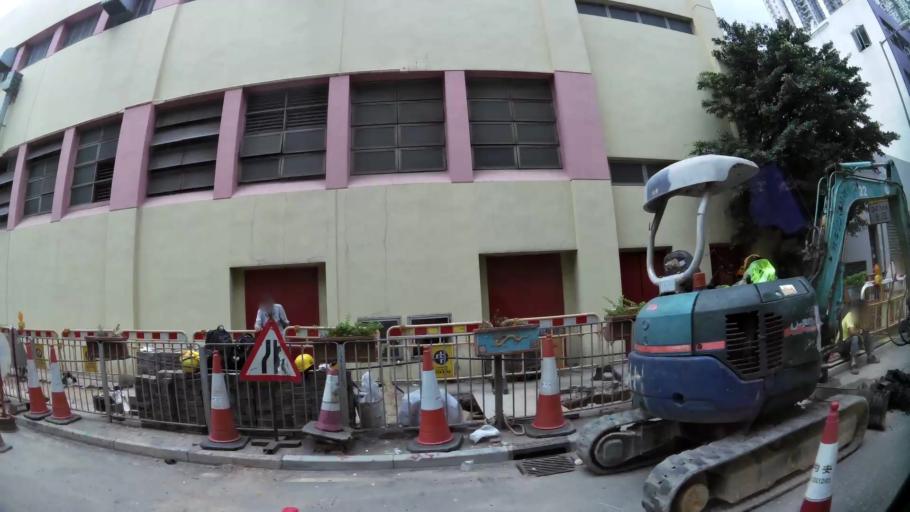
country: HK
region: Kowloon City
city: Kowloon
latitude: 22.3210
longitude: 114.1940
